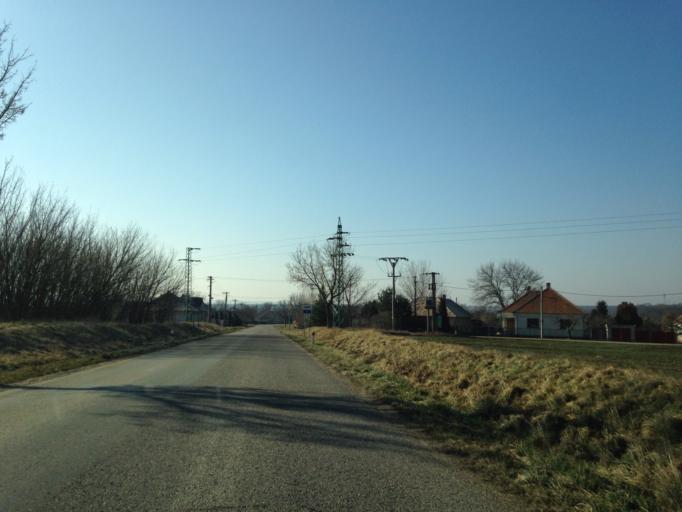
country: SK
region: Nitriansky
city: Svodin
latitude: 47.9353
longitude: 18.4060
